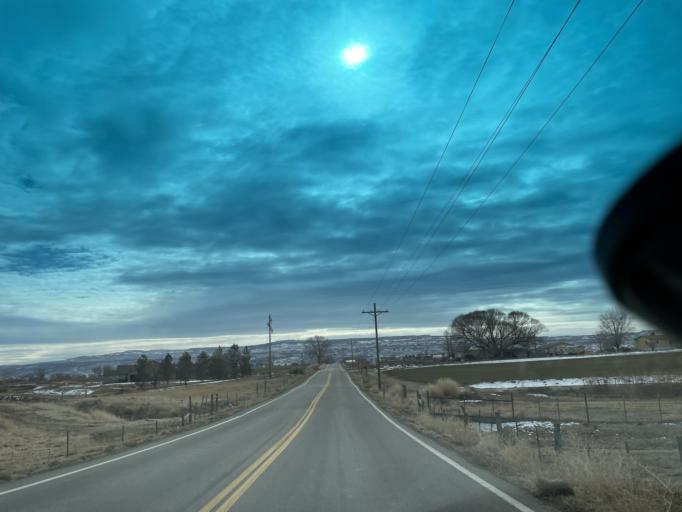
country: US
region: Colorado
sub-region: Mesa County
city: Loma
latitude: 39.2200
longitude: -108.8130
